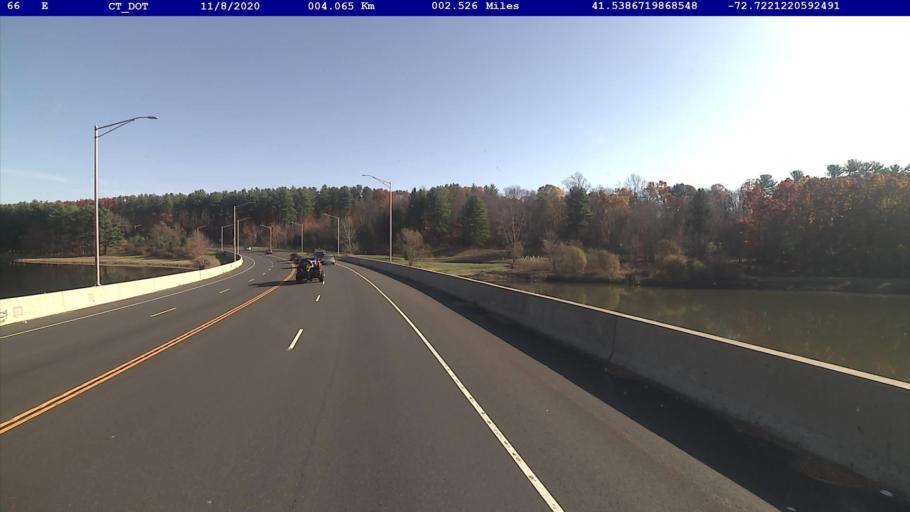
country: US
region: Connecticut
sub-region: Middlesex County
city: Durham
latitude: 41.5399
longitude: -72.7230
